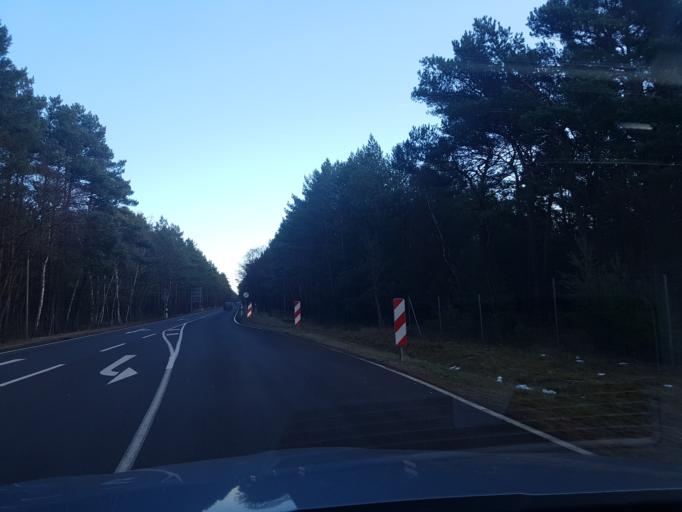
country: DE
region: Brandenburg
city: Kasel-Golzig
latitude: 52.0172
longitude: 13.7009
